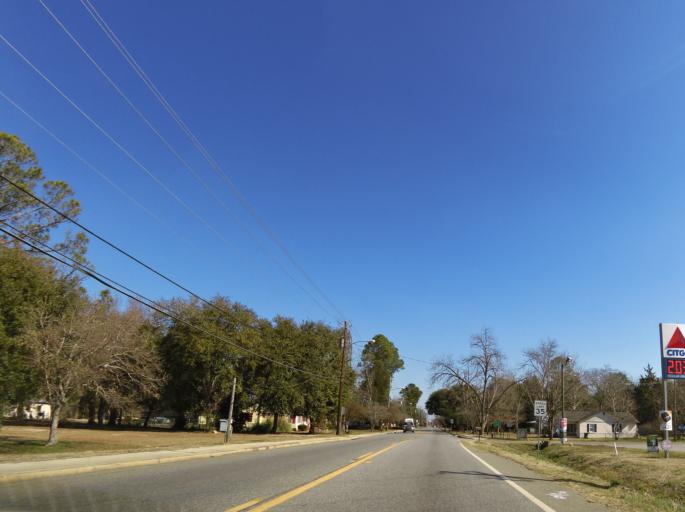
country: US
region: Georgia
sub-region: Bleckley County
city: Cochran
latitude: 32.3785
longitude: -83.3641
